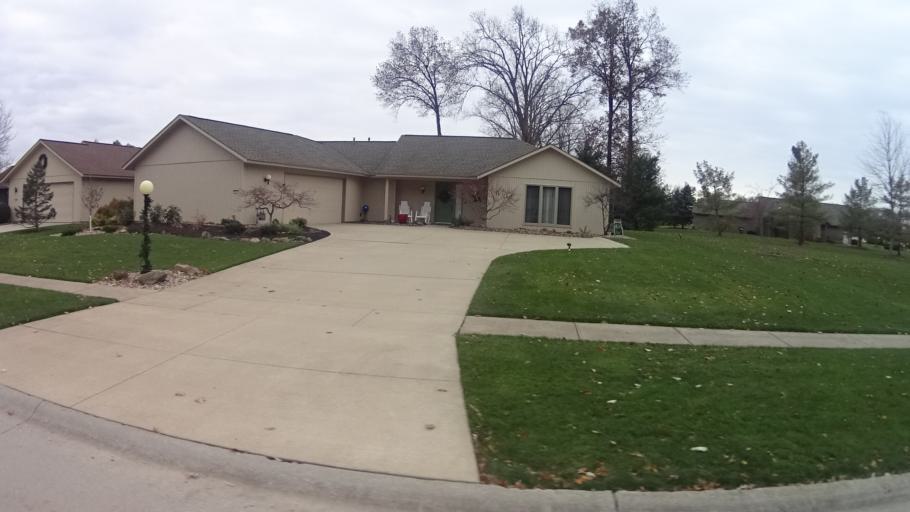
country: US
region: Ohio
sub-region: Lorain County
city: North Ridgeville
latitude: 41.3687
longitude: -81.9873
